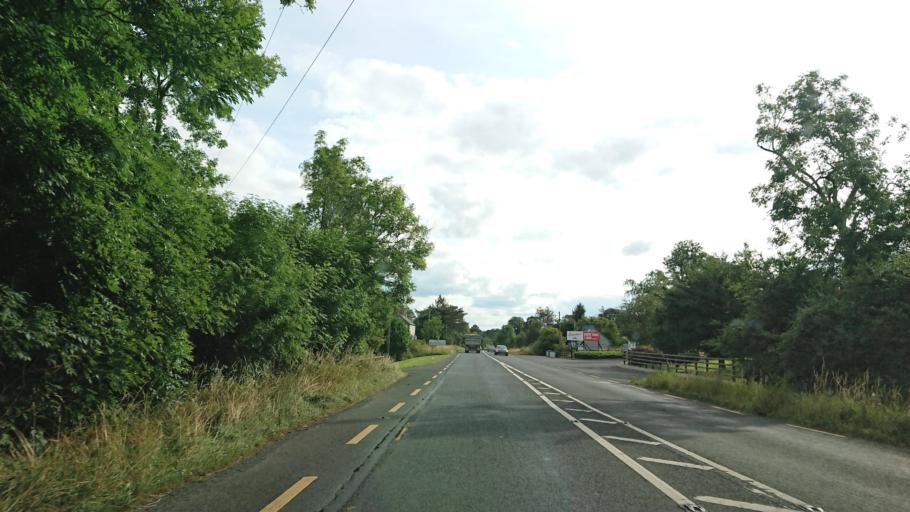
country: IE
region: Connaught
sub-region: County Leitrim
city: Carrick-on-Shannon
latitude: 53.9725
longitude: -8.0630
